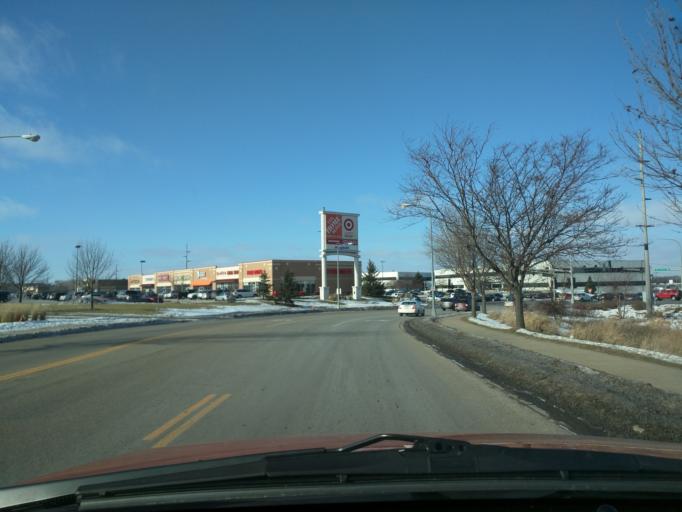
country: US
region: Minnesota
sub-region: Olmsted County
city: Rochester
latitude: 44.0644
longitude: -92.5026
